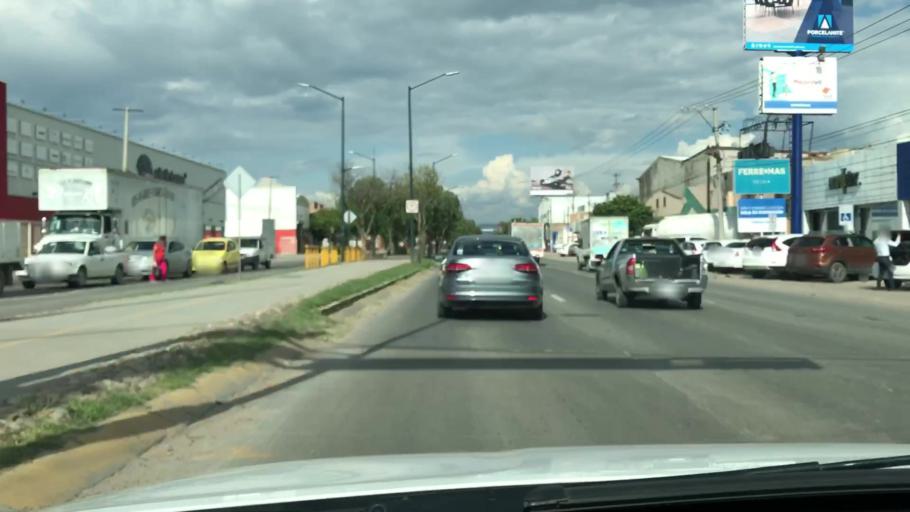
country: MX
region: Guanajuato
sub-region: Leon
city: Centro Familiar la Soledad
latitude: 21.0988
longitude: -101.7220
